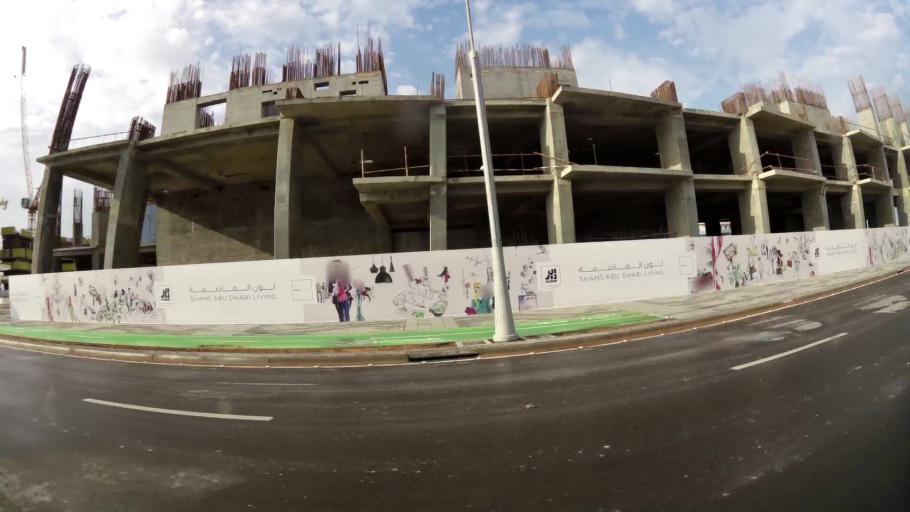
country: AE
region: Abu Dhabi
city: Abu Dhabi
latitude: 24.5090
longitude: 54.4090
